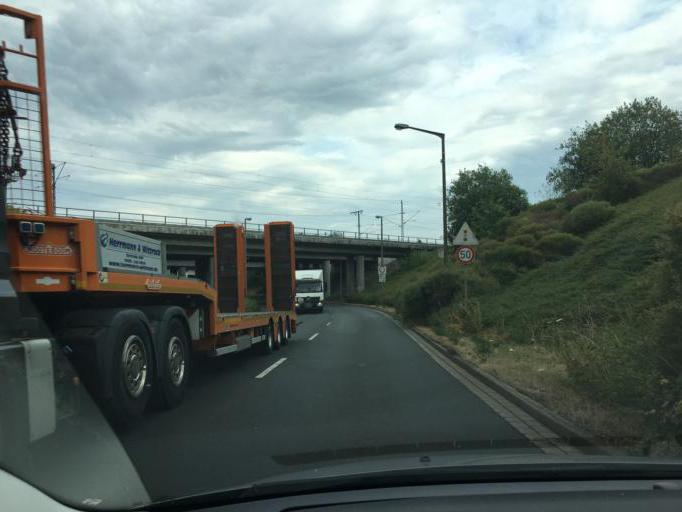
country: DE
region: Saxony
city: Rackwitz
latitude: 51.3945
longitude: 12.3889
